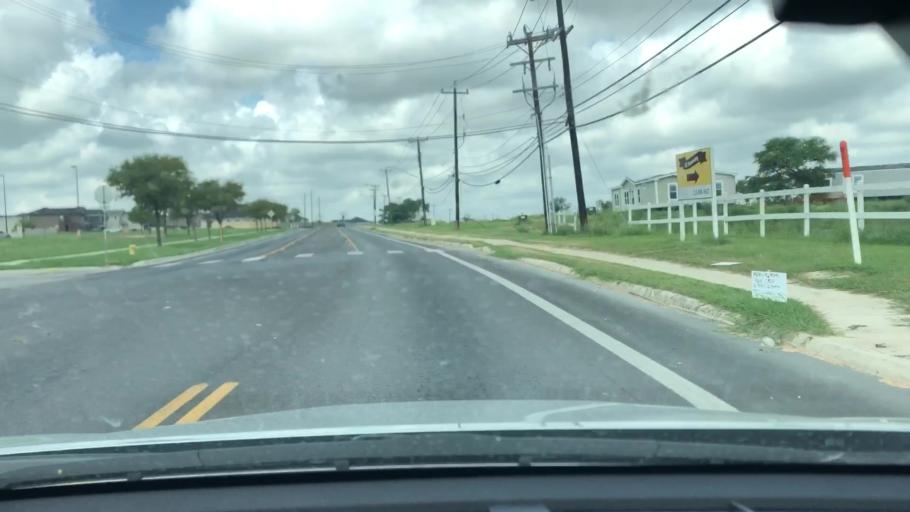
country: US
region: Texas
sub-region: Bexar County
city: Windcrest
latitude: 29.4969
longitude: -98.3627
